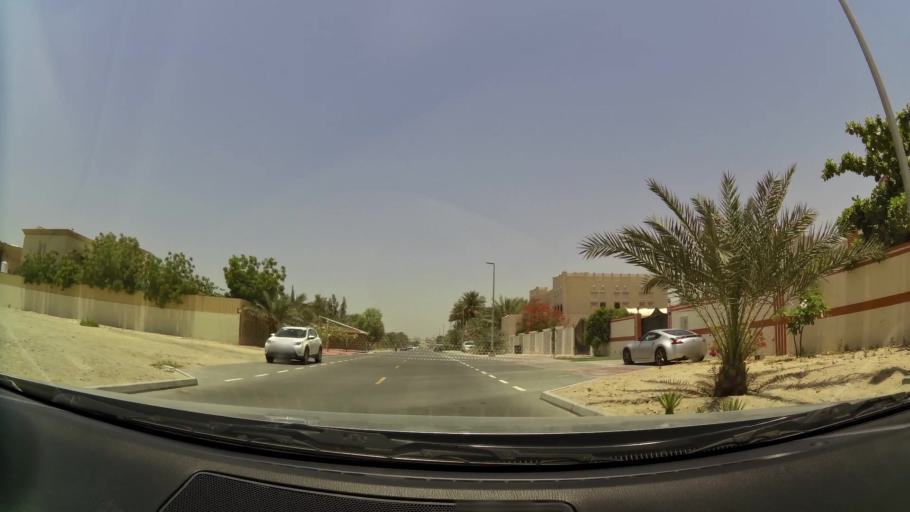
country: AE
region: Dubai
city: Dubai
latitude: 25.0932
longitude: 55.1887
